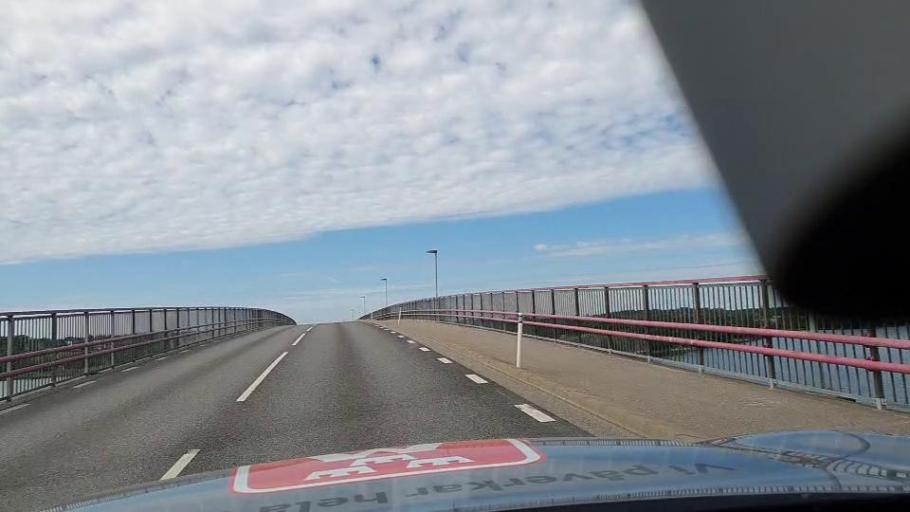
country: SE
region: Blekinge
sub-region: Karlskrona Kommun
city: Sturko
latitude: 56.1402
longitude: 15.7488
